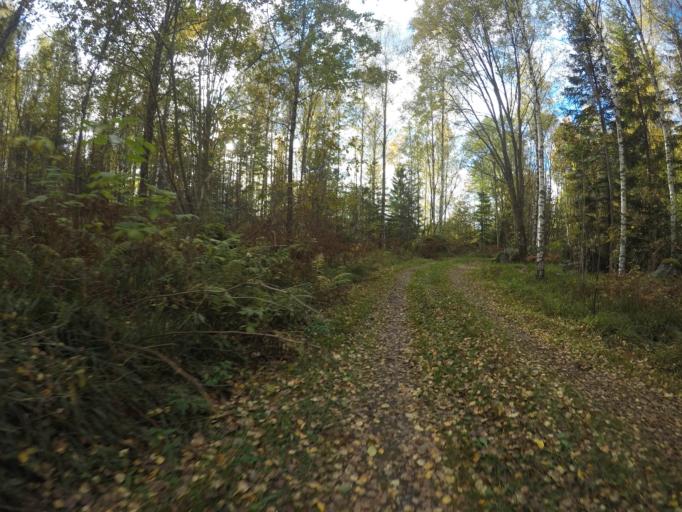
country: SE
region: Vaestmanland
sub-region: Arboga Kommun
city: Tyringe
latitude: 59.3755
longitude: 15.9475
